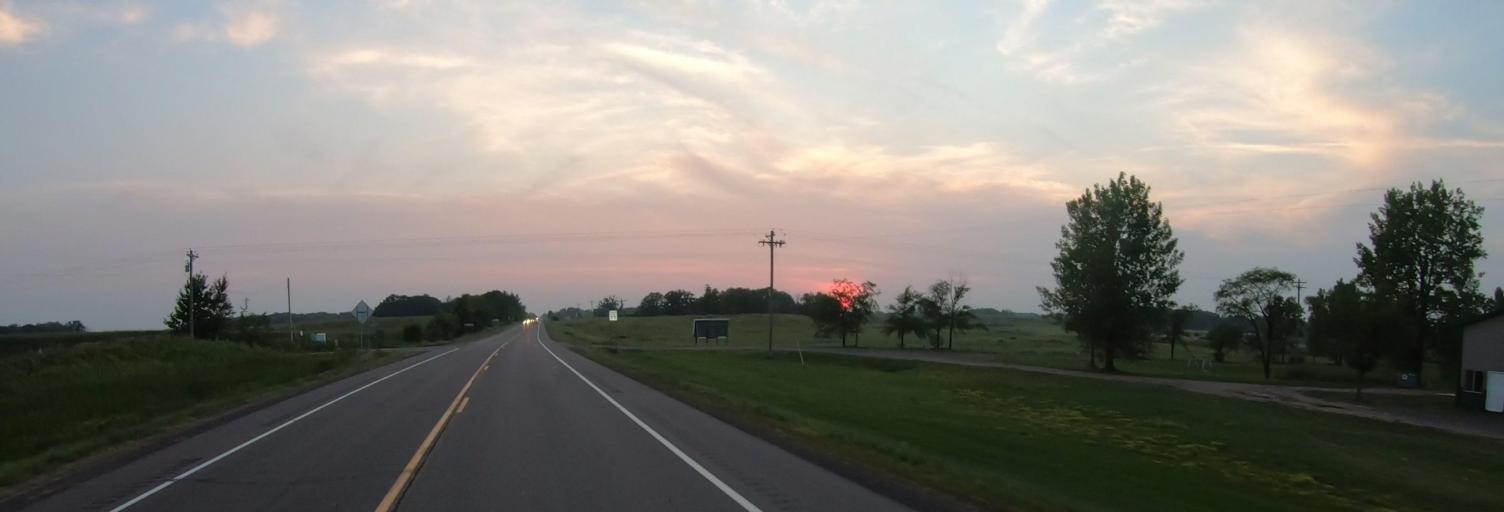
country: US
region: Minnesota
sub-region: Pine County
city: Rock Creek
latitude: 45.7666
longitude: -92.9696
